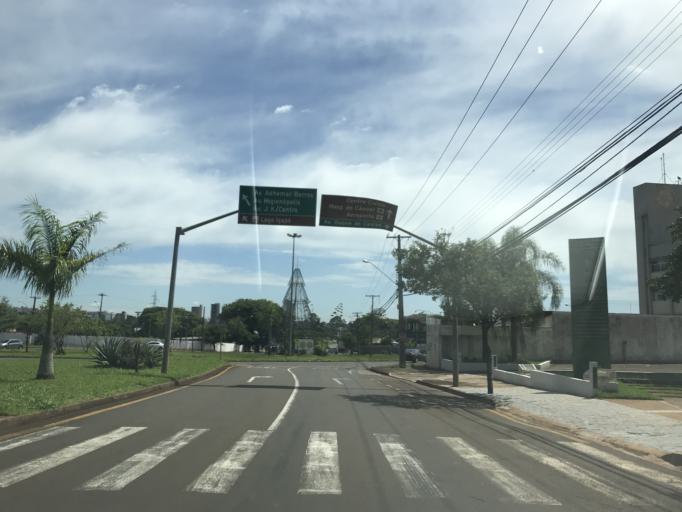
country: BR
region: Parana
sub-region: Londrina
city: Londrina
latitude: -23.3462
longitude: -51.1635
